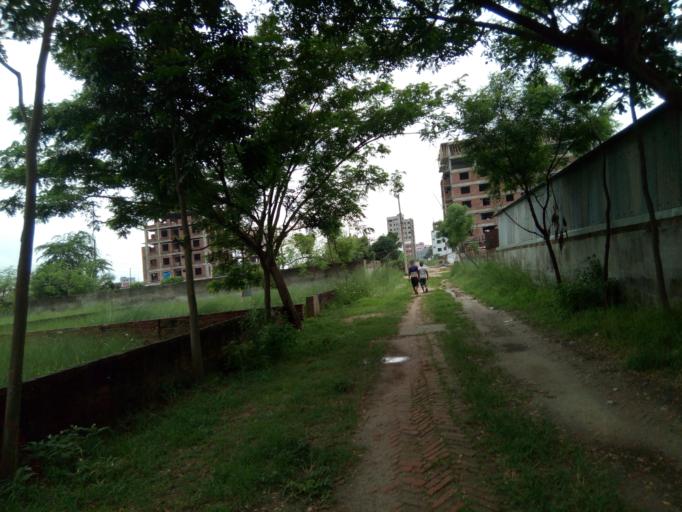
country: BD
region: Dhaka
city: Azimpur
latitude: 23.7491
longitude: 90.3488
